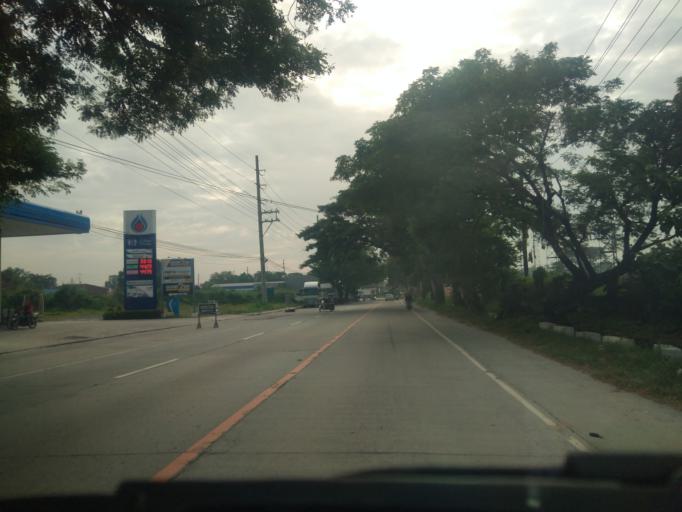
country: PH
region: Central Luzon
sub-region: Province of Pampanga
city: Calibutbut
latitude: 15.1163
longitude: 120.5944
